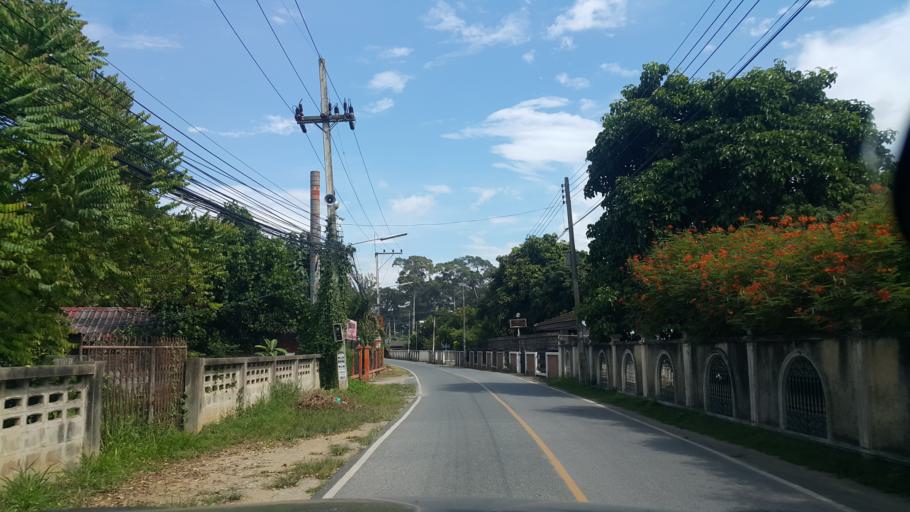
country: TH
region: Chiang Mai
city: Chiang Mai
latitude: 18.7502
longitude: 99.0067
